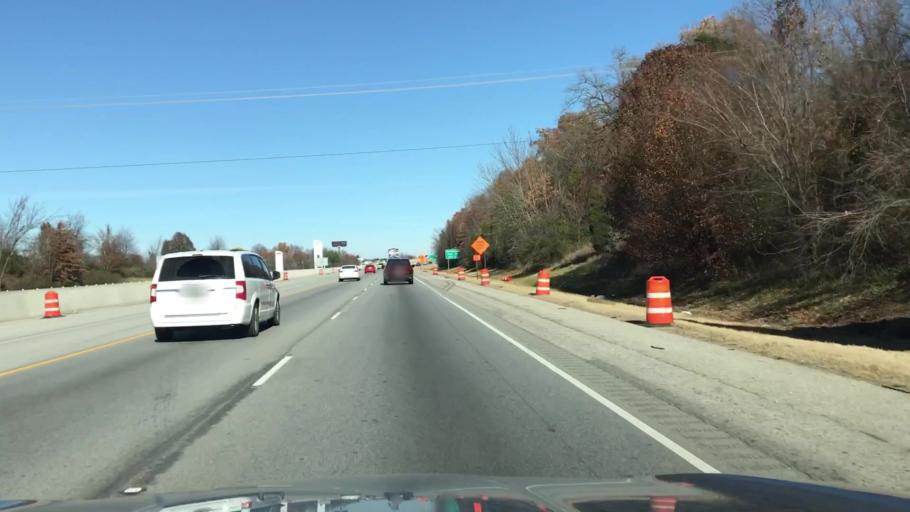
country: US
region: Arkansas
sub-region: Benton County
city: Bentonville
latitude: 36.3276
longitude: -94.1845
